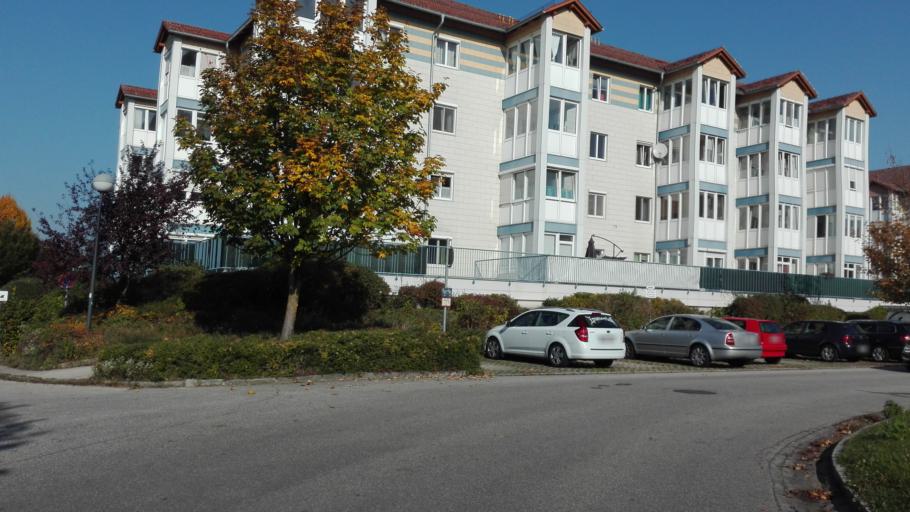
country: AT
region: Upper Austria
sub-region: Politischer Bezirk Linz-Land
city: Leonding
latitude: 48.2579
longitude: 14.2506
